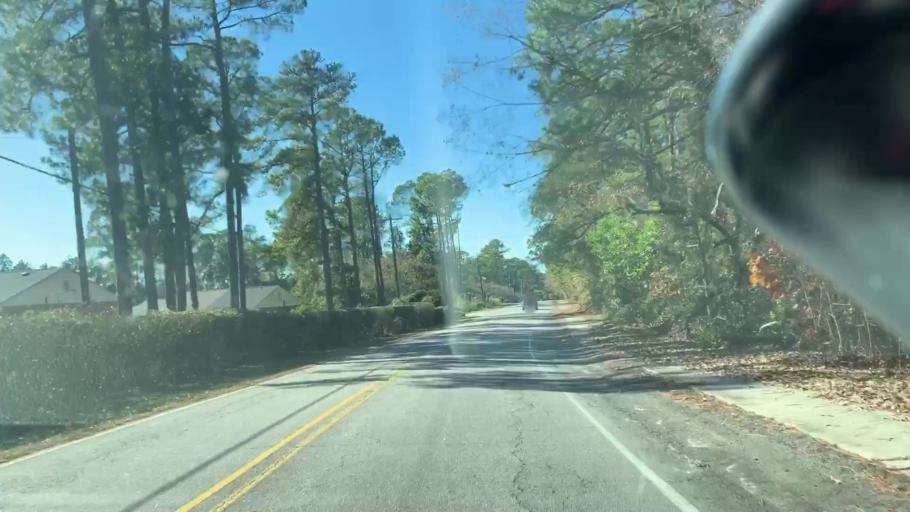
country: US
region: South Carolina
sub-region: Richland County
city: Woodfield
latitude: 34.0628
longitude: -80.9399
